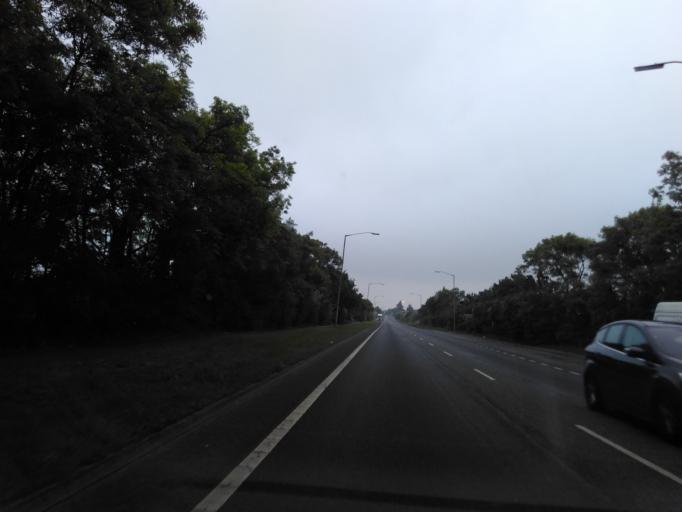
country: GB
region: England
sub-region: Kent
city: Whitstable
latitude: 51.3423
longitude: 1.0296
